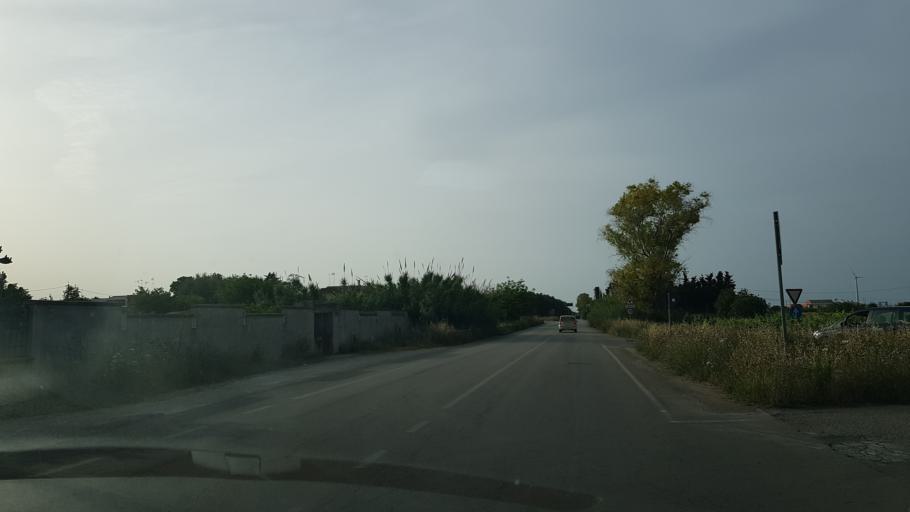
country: IT
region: Apulia
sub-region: Provincia di Brindisi
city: Tuturano
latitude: 40.5484
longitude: 17.9765
